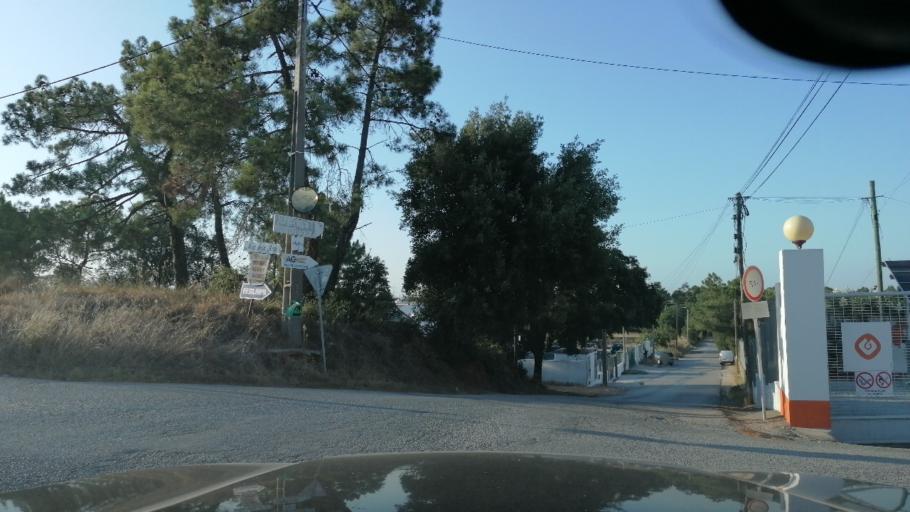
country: PT
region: Setubal
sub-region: Setubal
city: Setubal
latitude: 38.5401
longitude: -8.8423
